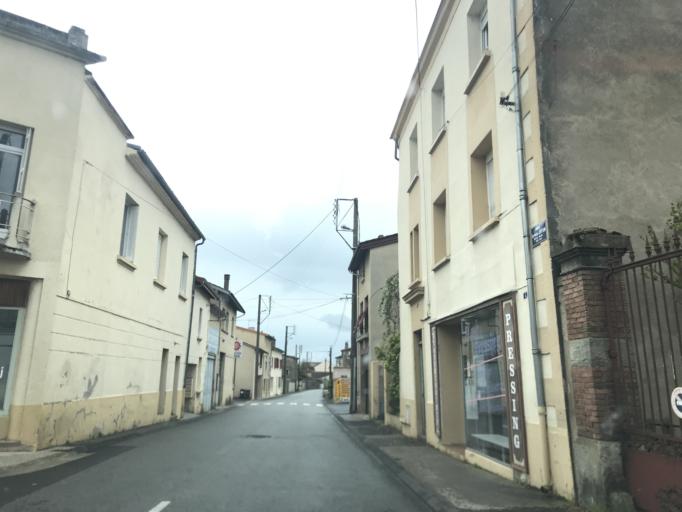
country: FR
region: Auvergne
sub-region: Departement du Puy-de-Dome
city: Lezoux
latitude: 45.8255
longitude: 3.3795
